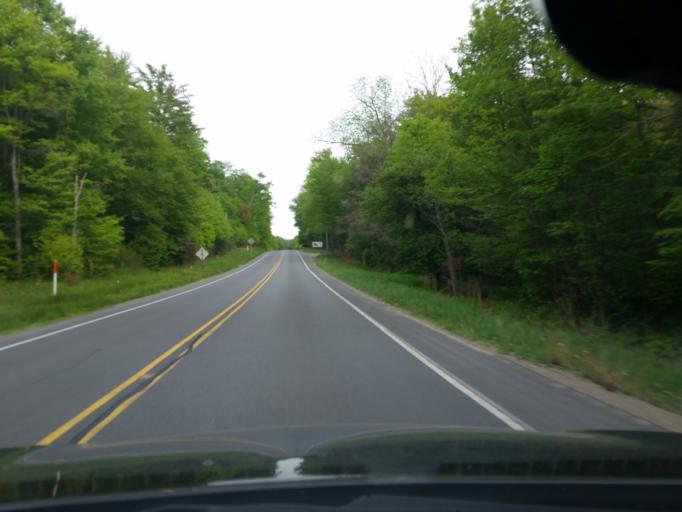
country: US
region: Pennsylvania
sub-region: McKean County
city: Kane
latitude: 41.5789
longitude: -78.9293
